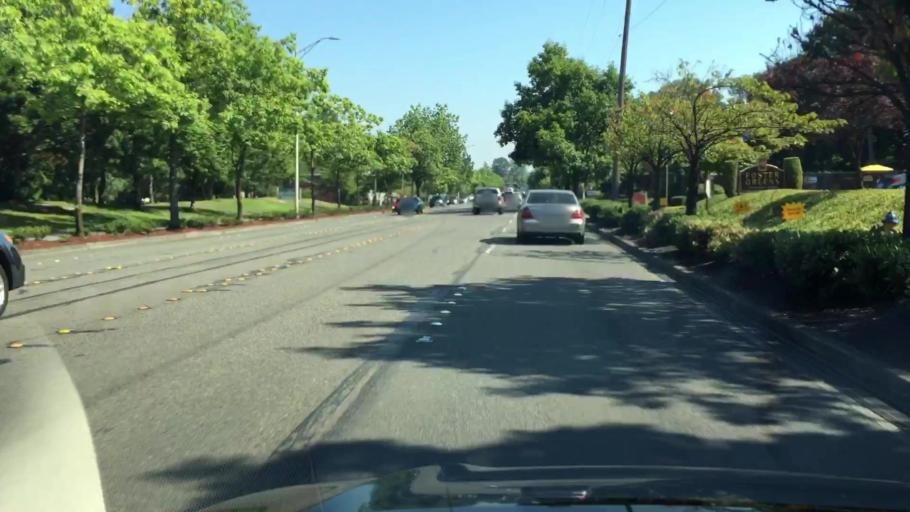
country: US
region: Washington
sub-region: King County
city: Tukwila
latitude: 47.4795
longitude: -122.2639
